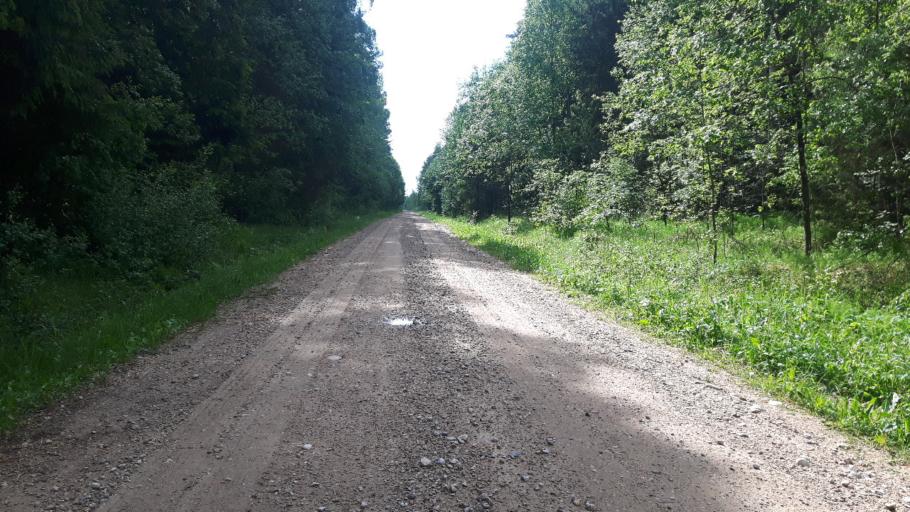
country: EE
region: Paernumaa
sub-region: Vaendra vald (alev)
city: Vandra
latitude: 58.7376
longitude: 24.9949
